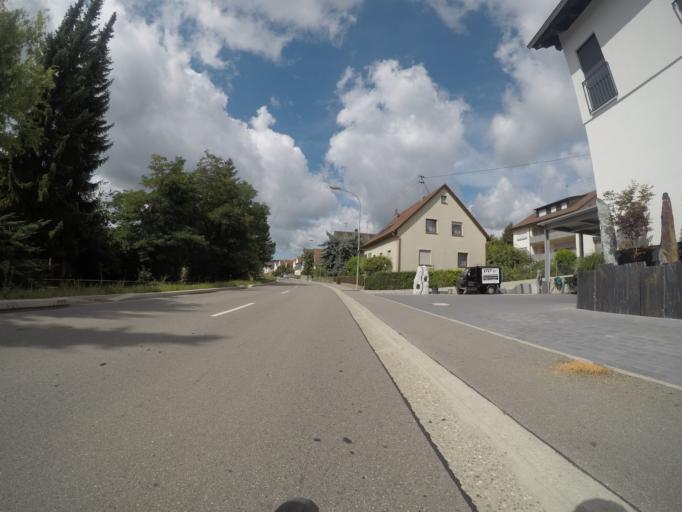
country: DE
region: Baden-Wuerttemberg
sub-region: Regierungsbezirk Stuttgart
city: Aidlingen
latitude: 48.6797
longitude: 8.8919
